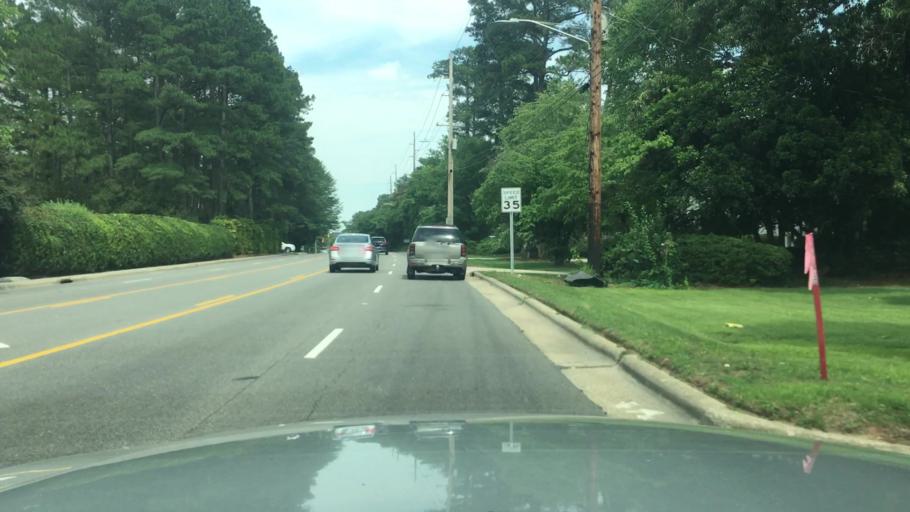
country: US
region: North Carolina
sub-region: Cumberland County
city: Fayetteville
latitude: 35.0640
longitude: -78.9354
